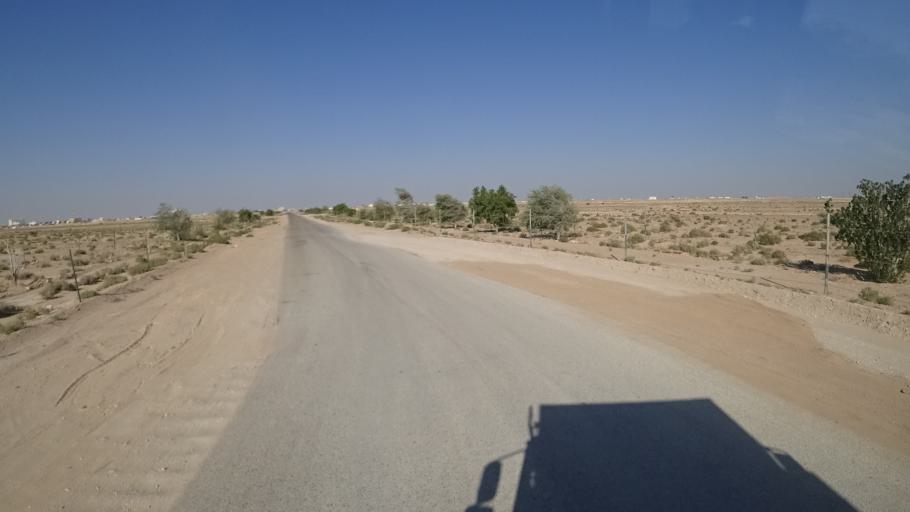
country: OM
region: Zufar
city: Salalah
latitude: 17.5942
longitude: 54.0324
